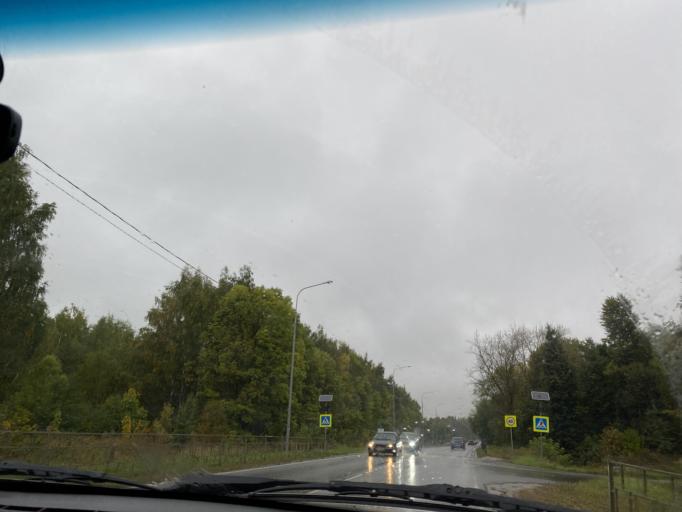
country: RU
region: Rjazan
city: Starozhilovo
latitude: 54.4450
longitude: 39.8893
